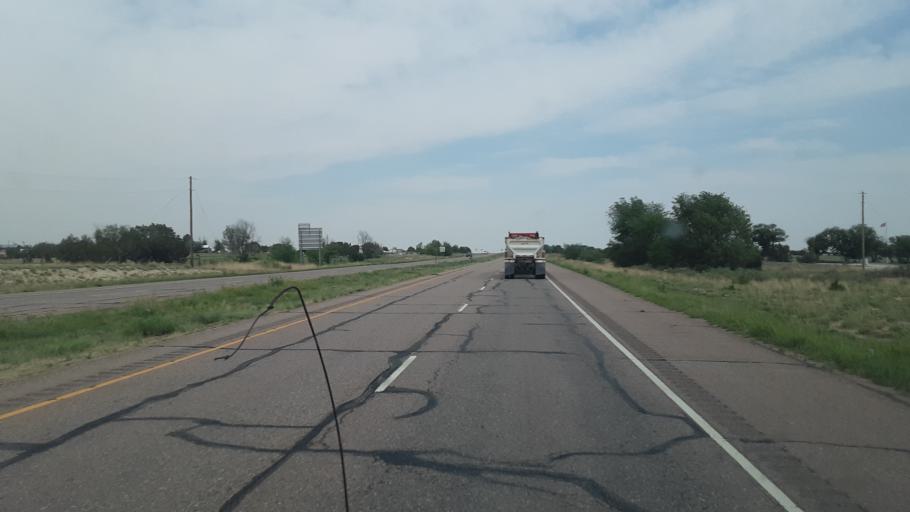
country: US
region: Colorado
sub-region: Fremont County
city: Penrose
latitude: 38.4151
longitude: -105.0287
